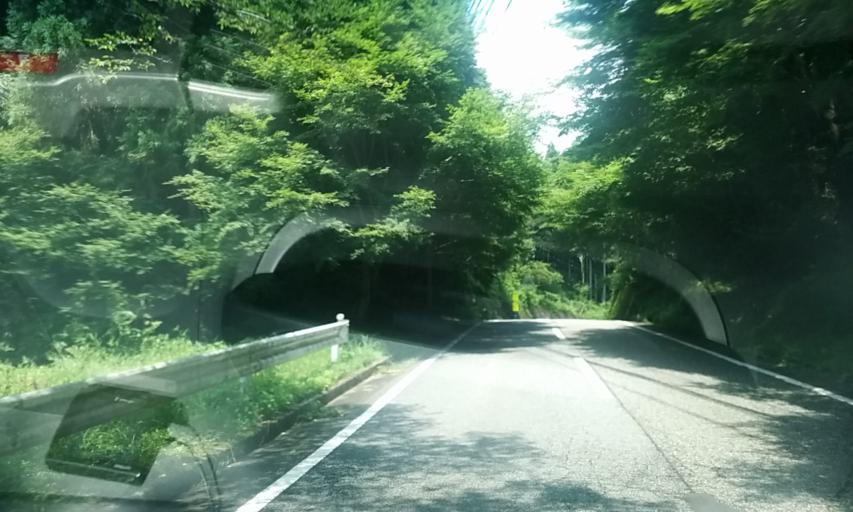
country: JP
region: Hyogo
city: Sasayama
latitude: 35.1738
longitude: 135.2472
